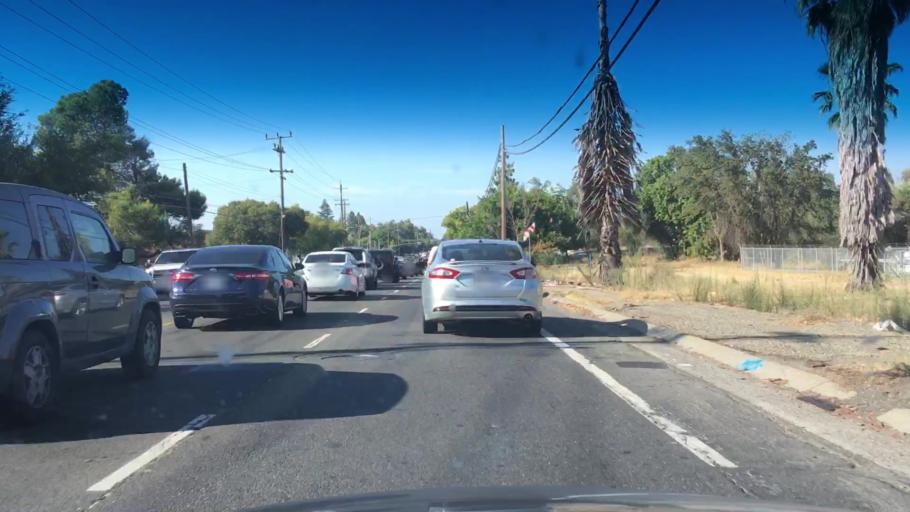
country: US
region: California
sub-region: Sacramento County
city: Orangevale
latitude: 38.6605
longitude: -121.2257
